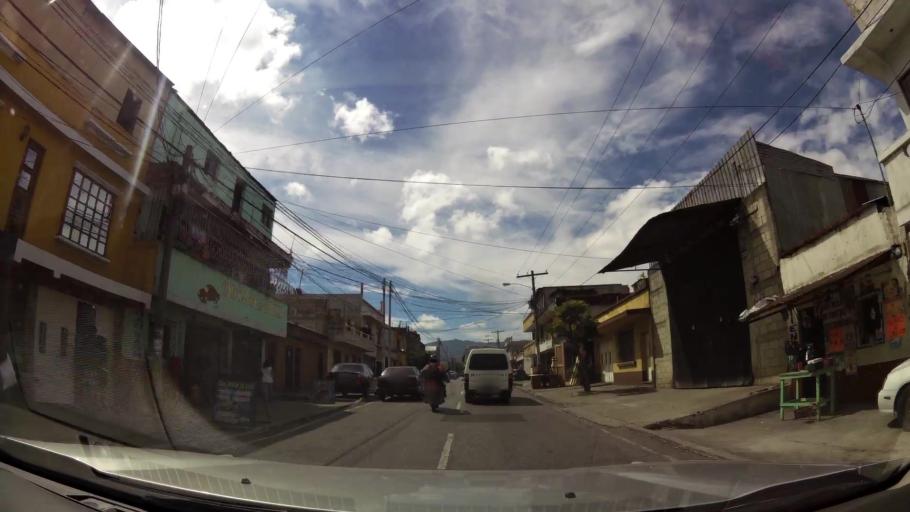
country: GT
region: Guatemala
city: Mixco
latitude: 14.6588
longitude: -90.5768
